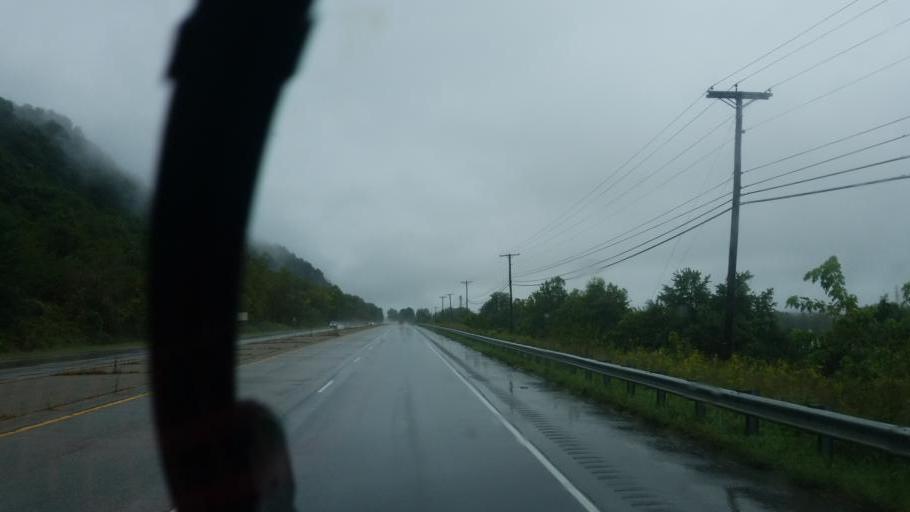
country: US
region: Ohio
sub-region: Scioto County
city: Portsmouth
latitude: 38.7219
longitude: -82.9809
